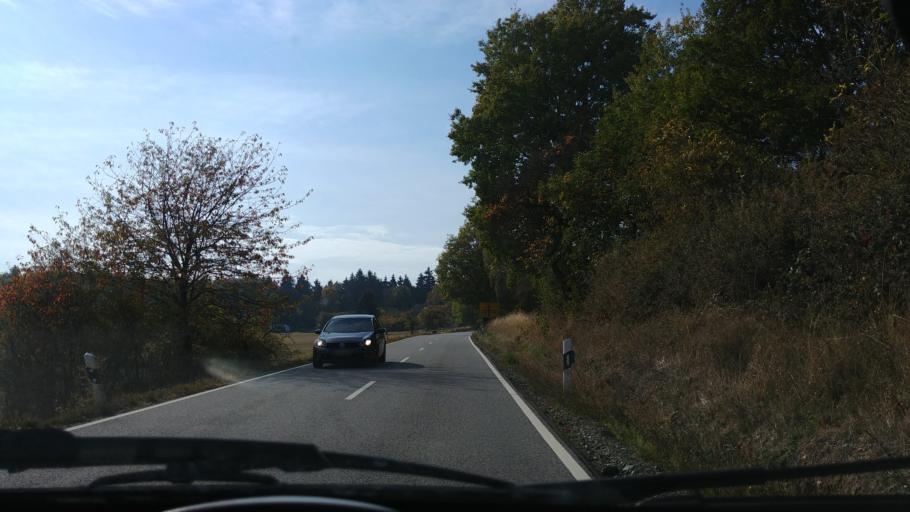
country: DE
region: Hesse
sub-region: Regierungsbezirk Darmstadt
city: Idstein
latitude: 50.1718
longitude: 8.2444
